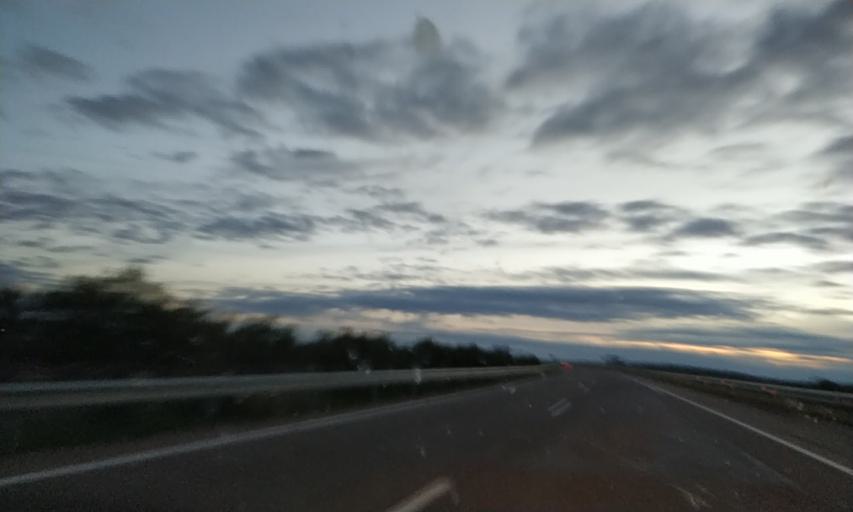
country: ES
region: Extremadura
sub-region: Provincia de Badajoz
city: Badajoz
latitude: 38.9203
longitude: -6.9678
